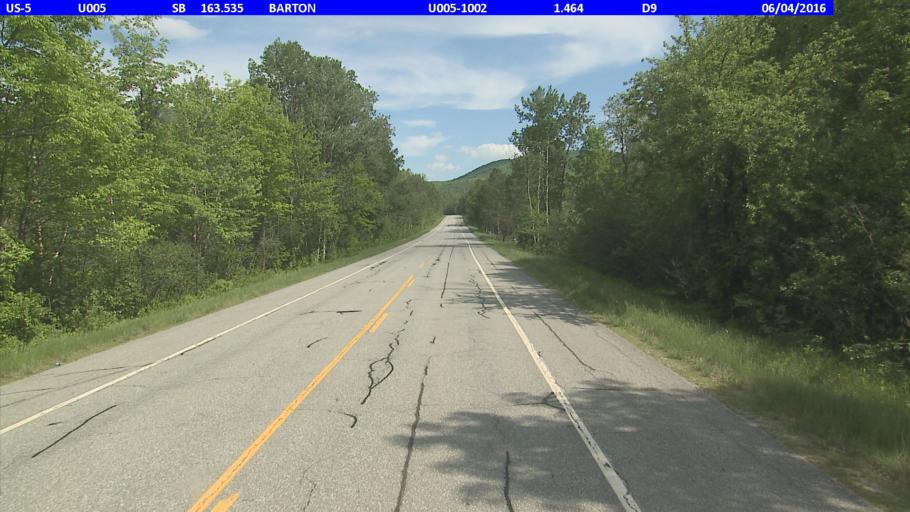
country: US
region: Vermont
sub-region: Caledonia County
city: Lyndonville
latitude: 44.7102
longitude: -72.1206
